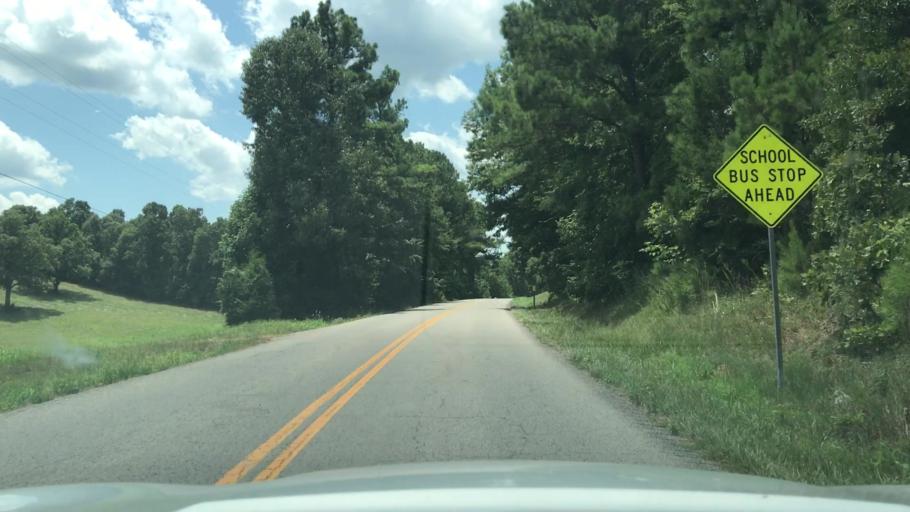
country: US
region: Kentucky
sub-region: Muhlenberg County
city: Greenville
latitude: 37.1374
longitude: -87.2666
